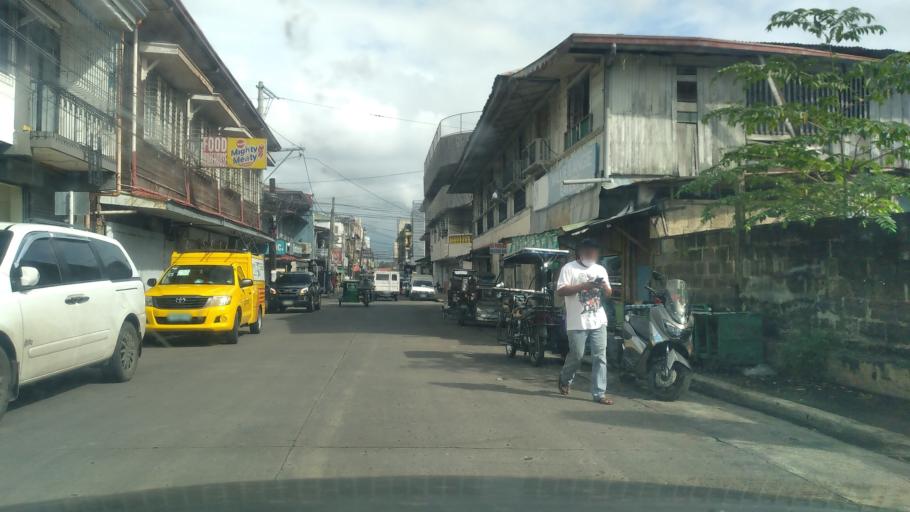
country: PH
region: Calabarzon
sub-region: Province of Quezon
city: Lucena
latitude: 13.9344
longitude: 121.6116
